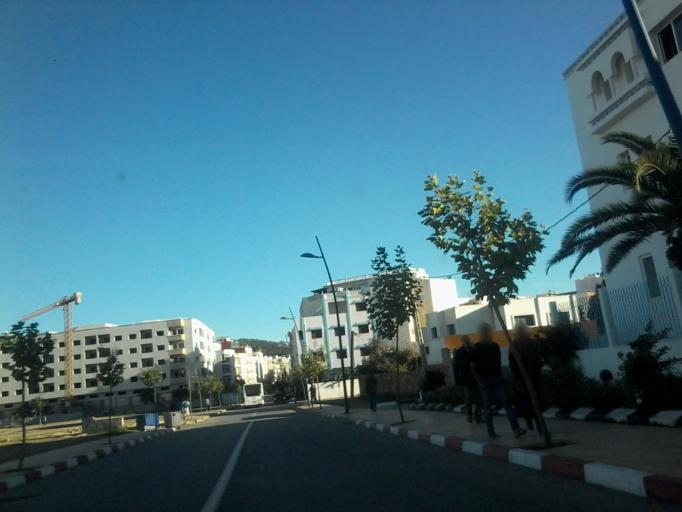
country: MA
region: Tanger-Tetouan
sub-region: Tetouan
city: Martil
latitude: 35.6889
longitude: -5.3283
